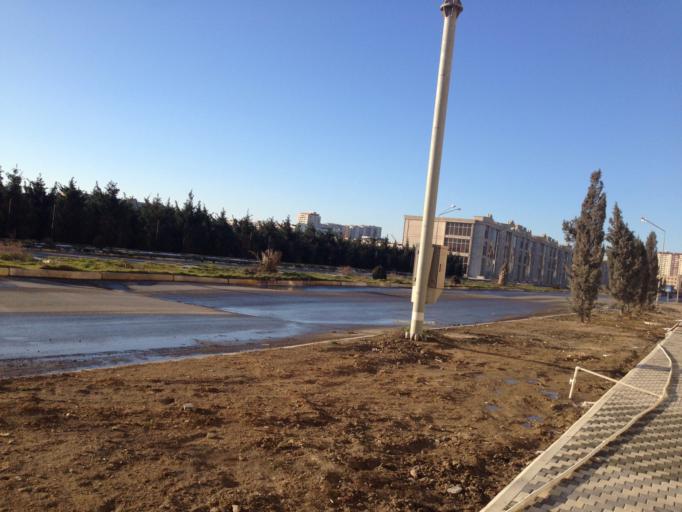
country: AZ
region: Baki
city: Baku
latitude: 40.4092
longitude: 49.8595
